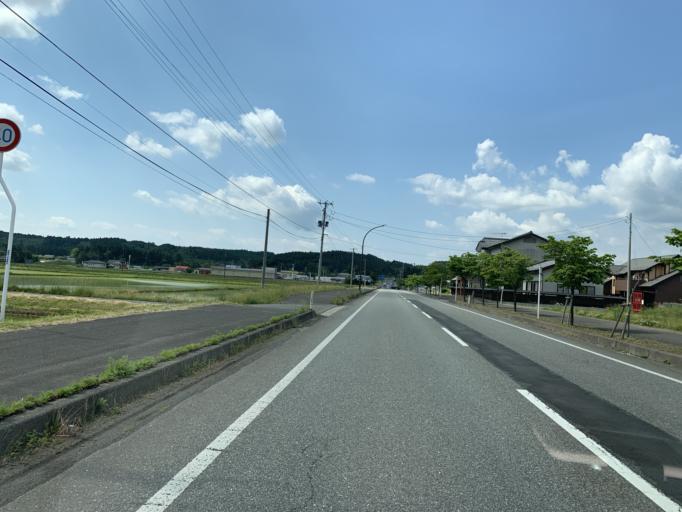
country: JP
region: Miyagi
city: Furukawa
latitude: 38.7378
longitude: 140.9596
